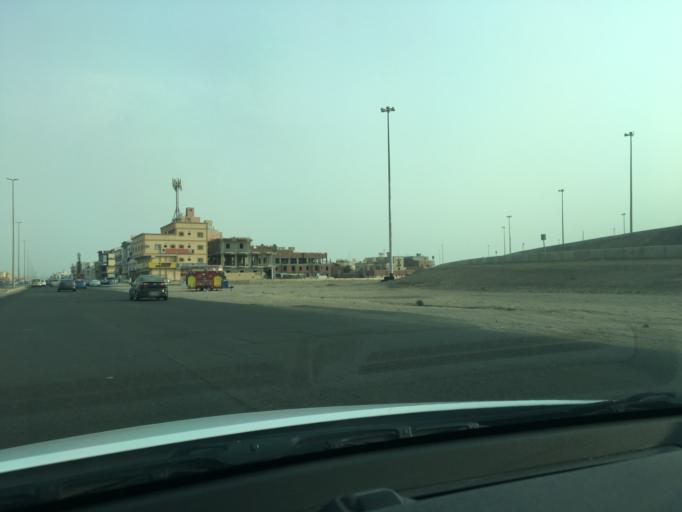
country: SA
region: Makkah
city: Jeddah
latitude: 21.7619
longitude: 39.1832
